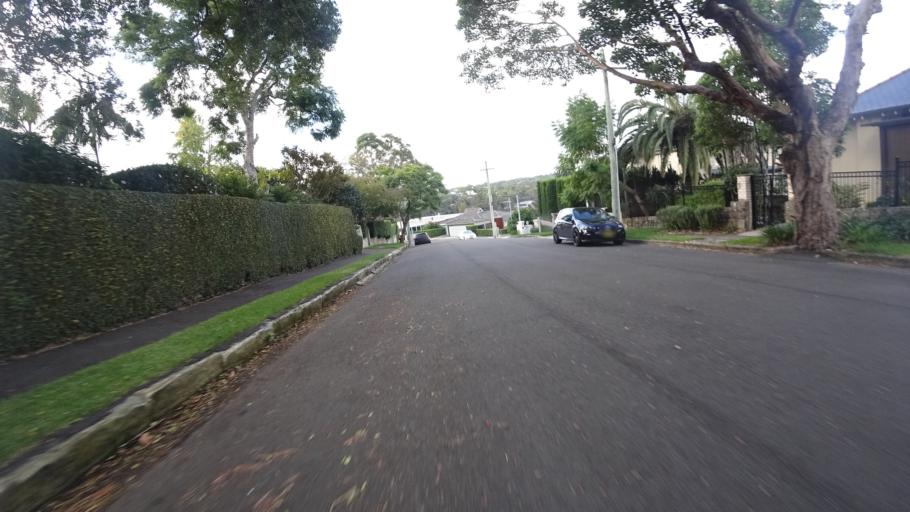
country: AU
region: New South Wales
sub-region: Lane Cove
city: Longueville
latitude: -33.8339
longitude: 151.1569
